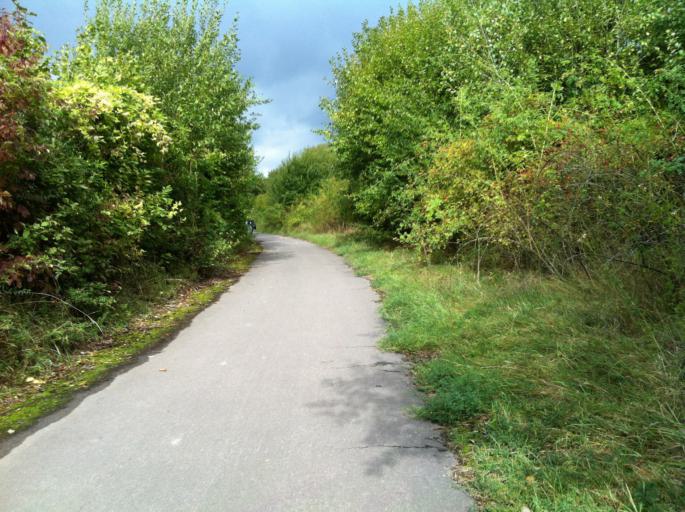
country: DE
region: Rheinland-Pfalz
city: Essenheim
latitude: 49.9562
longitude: 8.1569
